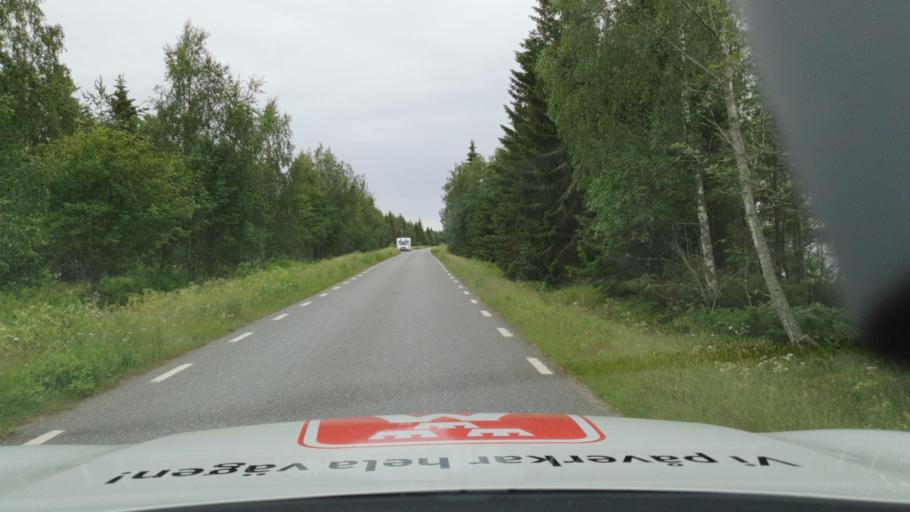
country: SE
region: Vaesterbotten
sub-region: Nordmalings Kommun
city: Nordmaling
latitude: 63.4656
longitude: 19.4649
